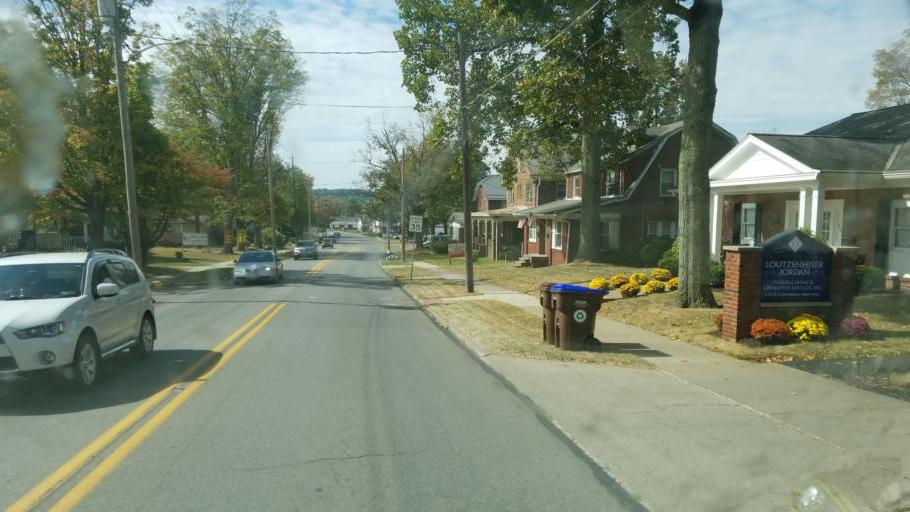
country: US
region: Pennsylvania
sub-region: Mercer County
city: Greenville
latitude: 41.4090
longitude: -80.3760
